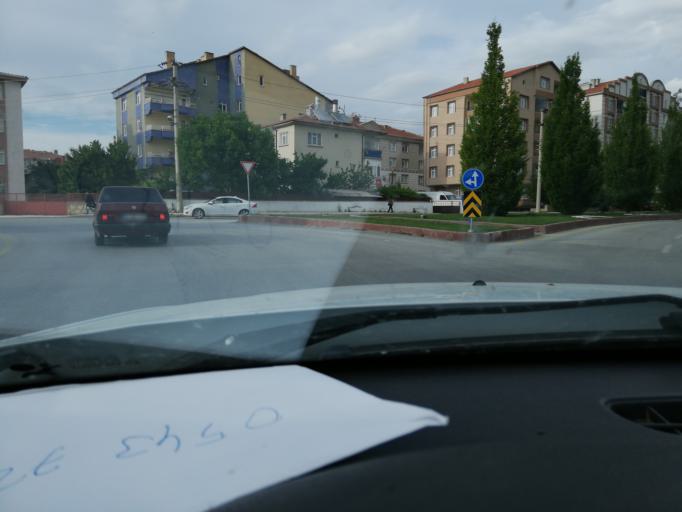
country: TR
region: Kirsehir
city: Kirsehir
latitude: 39.1350
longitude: 34.1599
